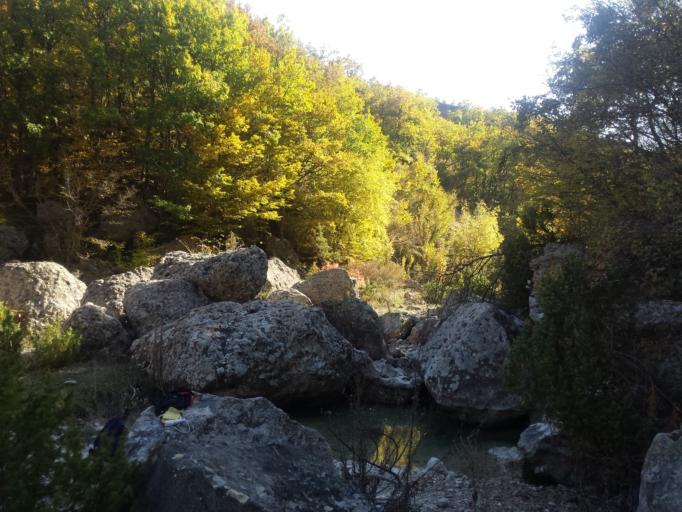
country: BG
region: Kurdzhali
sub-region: Obshtina Krumovgrad
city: Krumovgrad
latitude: 41.5626
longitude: 25.5329
